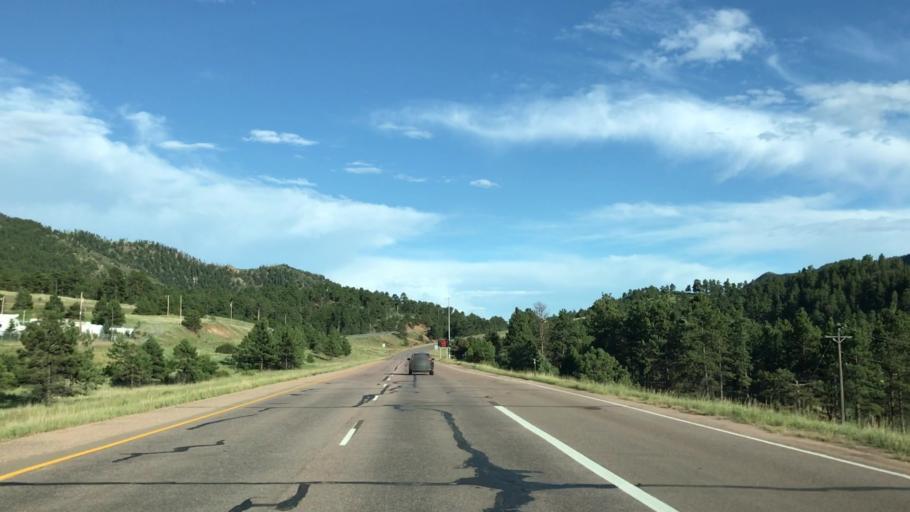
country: US
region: Colorado
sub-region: El Paso County
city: Cascade-Chipita Park
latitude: 38.9414
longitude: -105.0159
